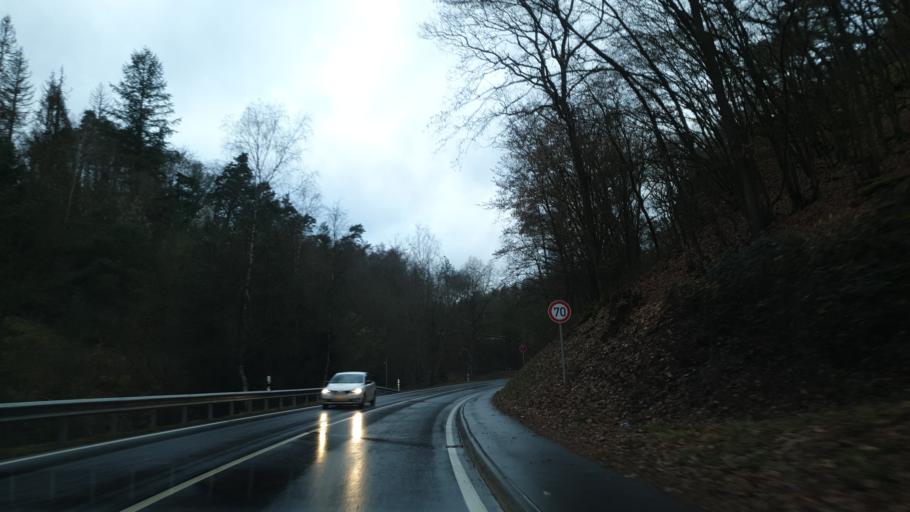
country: DE
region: Rheinland-Pfalz
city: Holzappel
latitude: 50.3379
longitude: 7.9023
